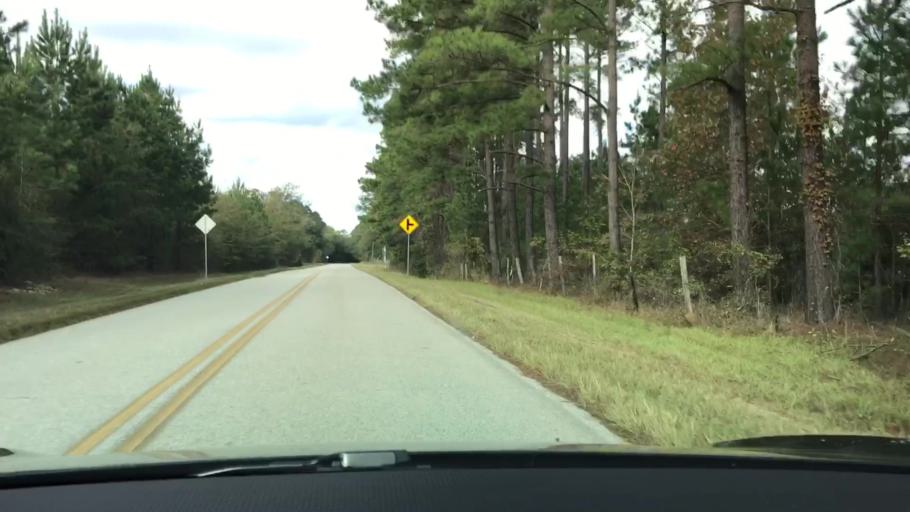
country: US
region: Georgia
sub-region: Jefferson County
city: Wadley
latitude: 32.8074
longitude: -82.3935
